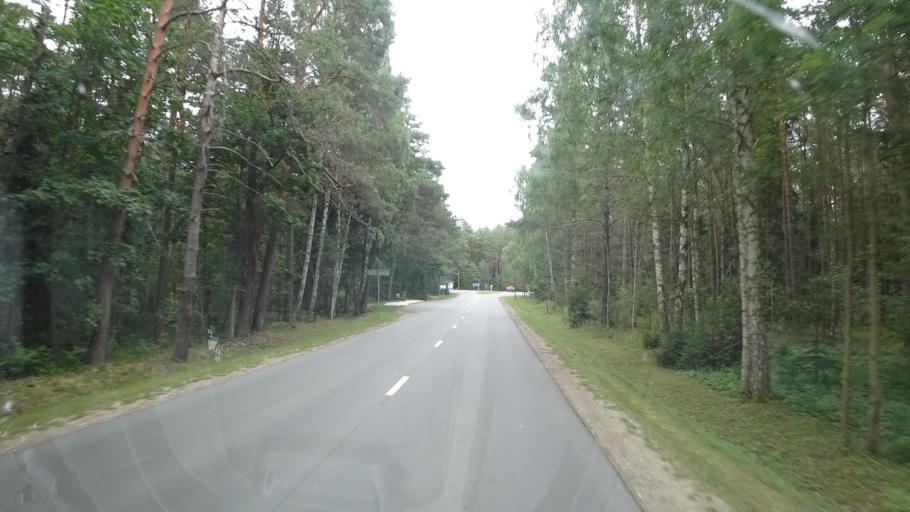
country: LT
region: Klaipedos apskritis
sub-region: Palanga
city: Sventoji
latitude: 56.0238
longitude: 21.1093
